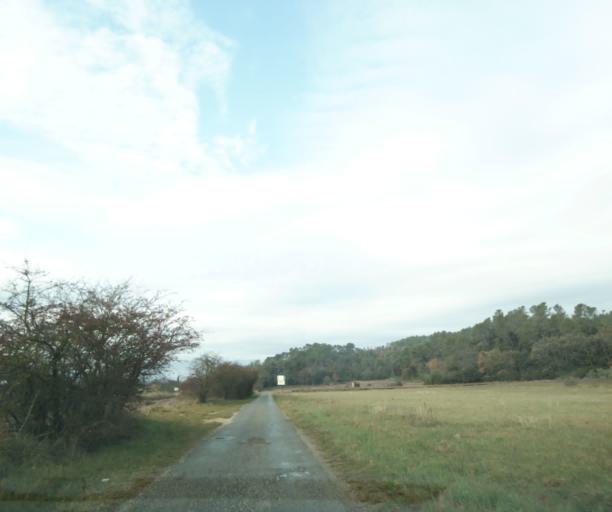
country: FR
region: Provence-Alpes-Cote d'Azur
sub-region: Departement du Var
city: Tourves
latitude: 43.4088
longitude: 5.9582
